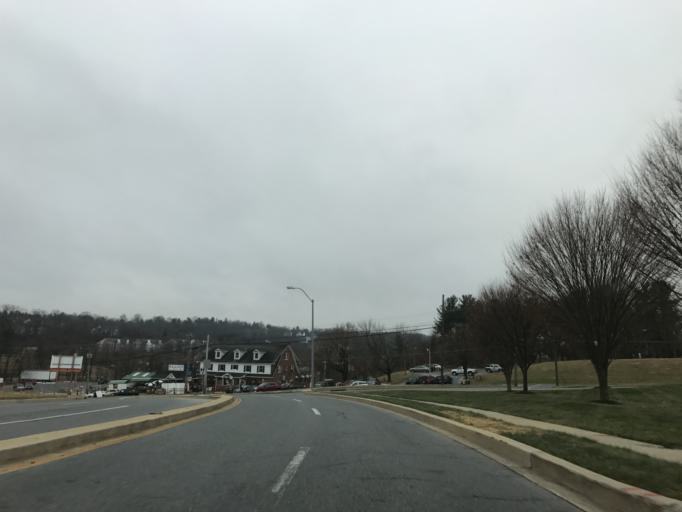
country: US
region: Maryland
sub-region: Carroll County
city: Westminster
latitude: 39.5857
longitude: -77.0113
